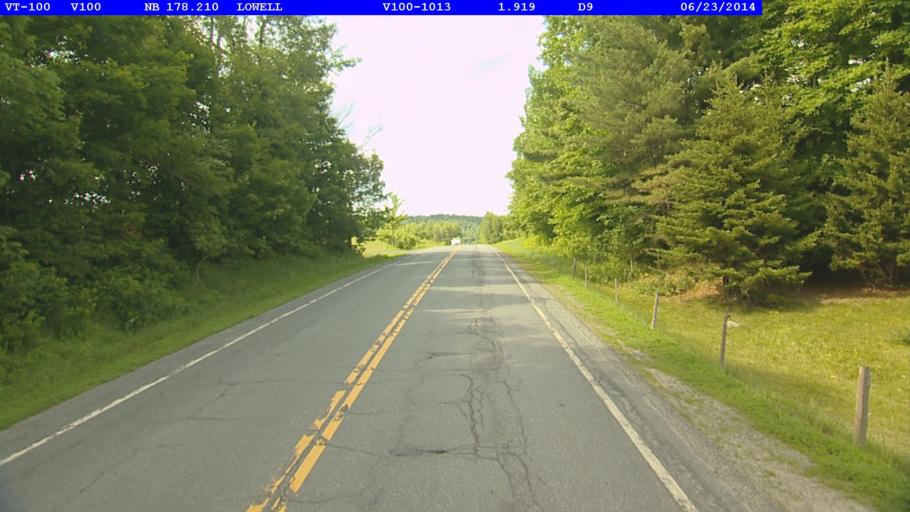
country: US
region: Vermont
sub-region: Lamoille County
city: Hyde Park
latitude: 44.7657
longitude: -72.4569
